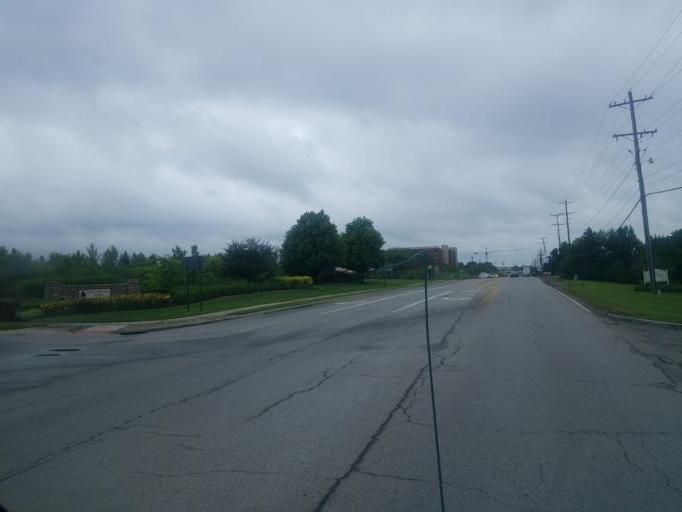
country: US
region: Ohio
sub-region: Franklin County
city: Reynoldsburg
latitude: 39.9862
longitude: -82.8431
